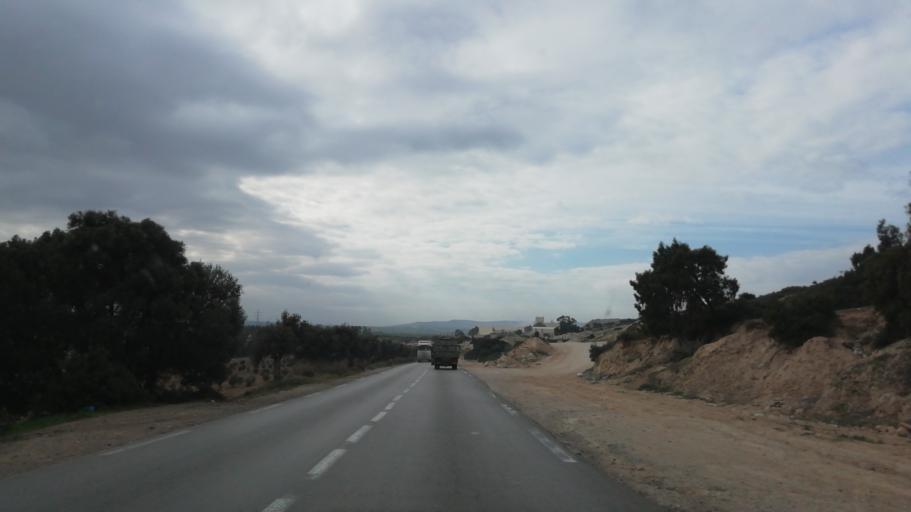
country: DZ
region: Oran
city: Ain el Bya
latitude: 35.7173
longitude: -0.3582
